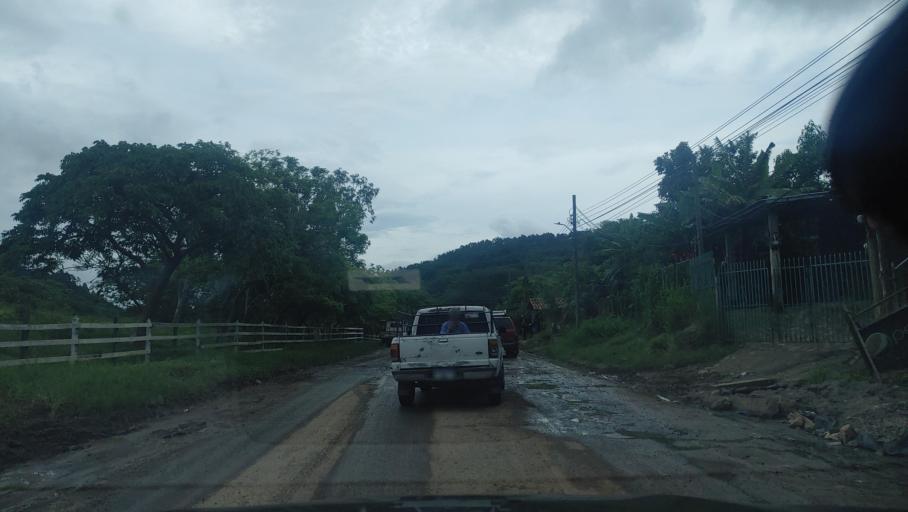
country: HN
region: Choluteca
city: San Marcos de Colon
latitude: 13.3796
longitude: -86.8726
